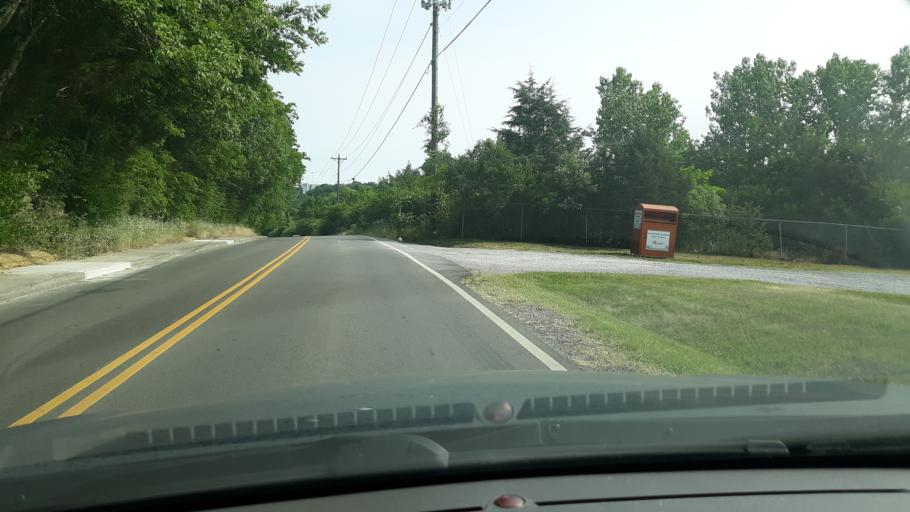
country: US
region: Tennessee
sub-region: Davidson County
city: Lakewood
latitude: 36.1857
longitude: -86.6082
